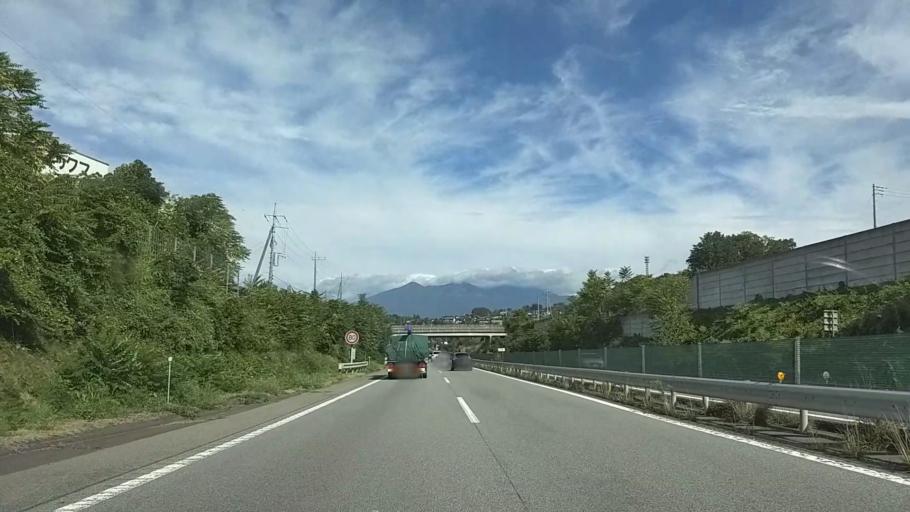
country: JP
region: Yamanashi
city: Nirasaki
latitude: 35.7507
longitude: 138.4420
